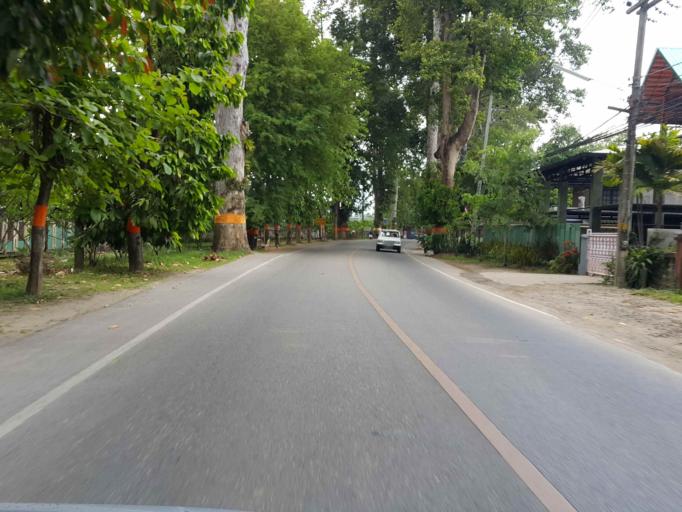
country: TH
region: Chiang Mai
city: Saraphi
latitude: 18.7031
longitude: 99.0410
